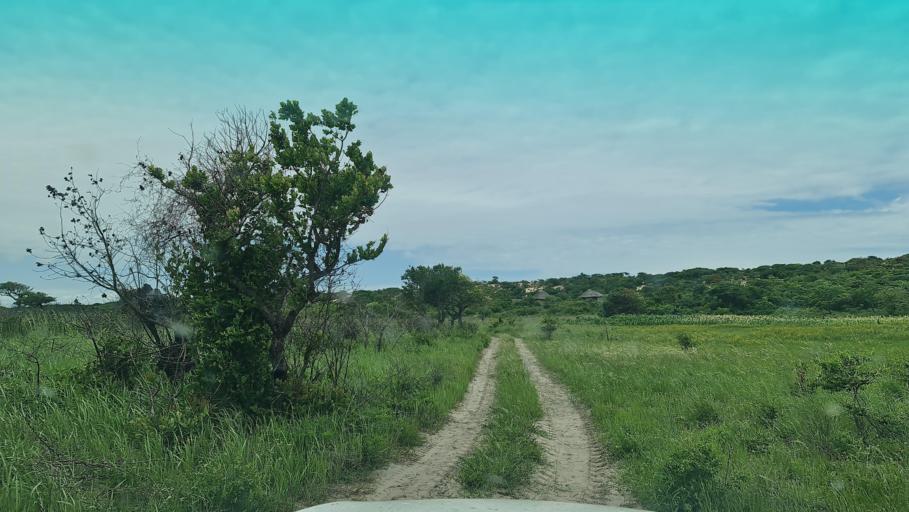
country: EG
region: Luxor
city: Luxor
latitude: 25.6376
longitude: 32.7724
